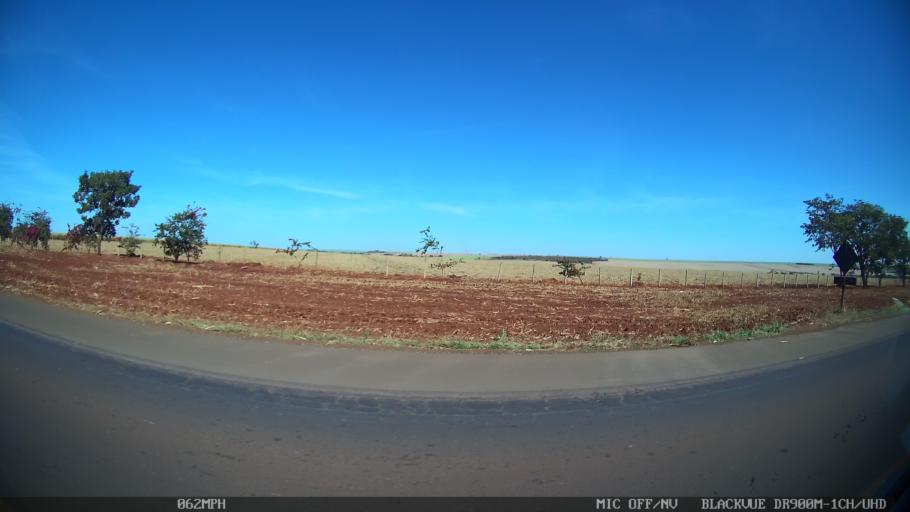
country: BR
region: Sao Paulo
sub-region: Ipua
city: Ipua
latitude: -20.4958
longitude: -47.9733
